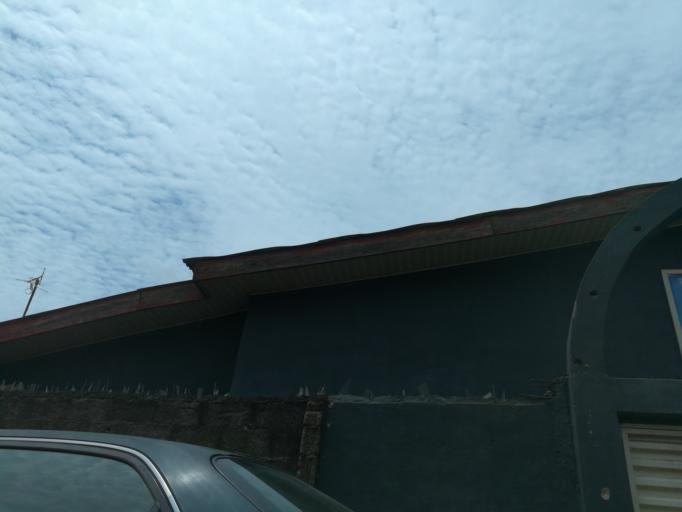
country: NG
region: Lagos
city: Oshodi
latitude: 6.5605
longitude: 3.3272
